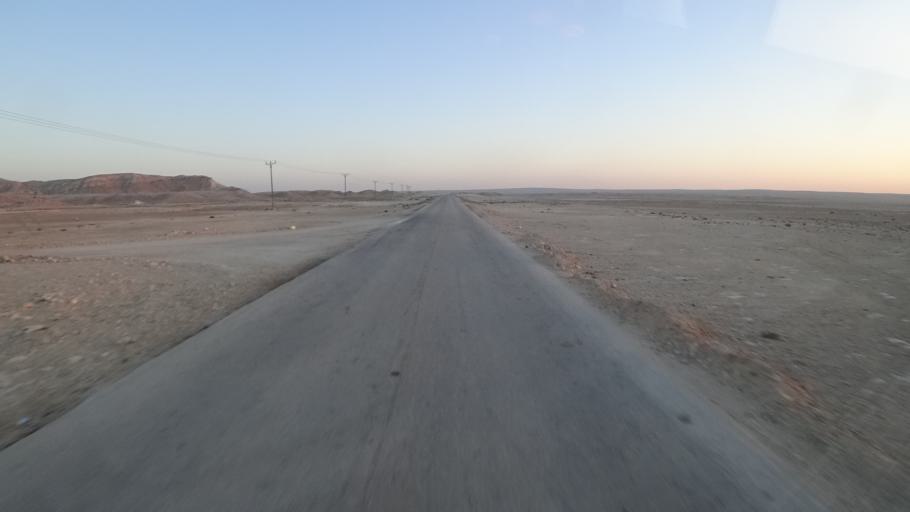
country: YE
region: Al Mahrah
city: Hawf
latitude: 16.9284
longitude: 53.3787
